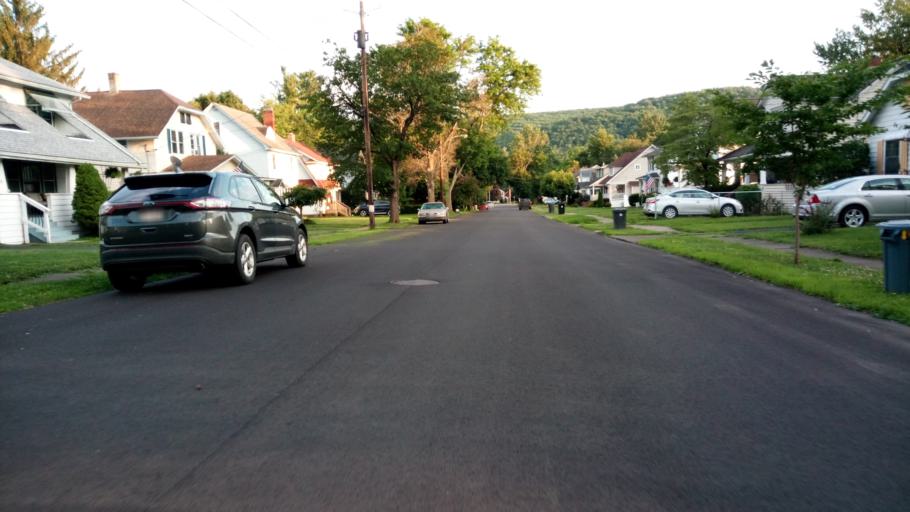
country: US
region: New York
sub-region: Chemung County
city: West Elmira
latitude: 42.0801
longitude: -76.8511
